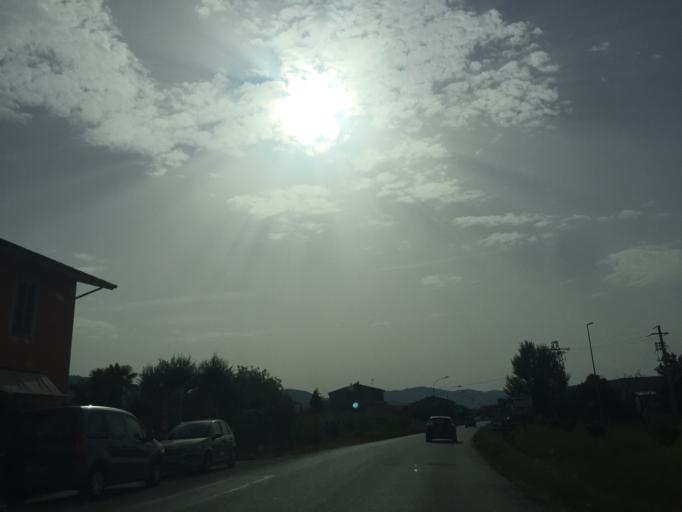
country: IT
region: Tuscany
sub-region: Provincia di Pistoia
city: Monsummano Terme
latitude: 43.8606
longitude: 10.7990
